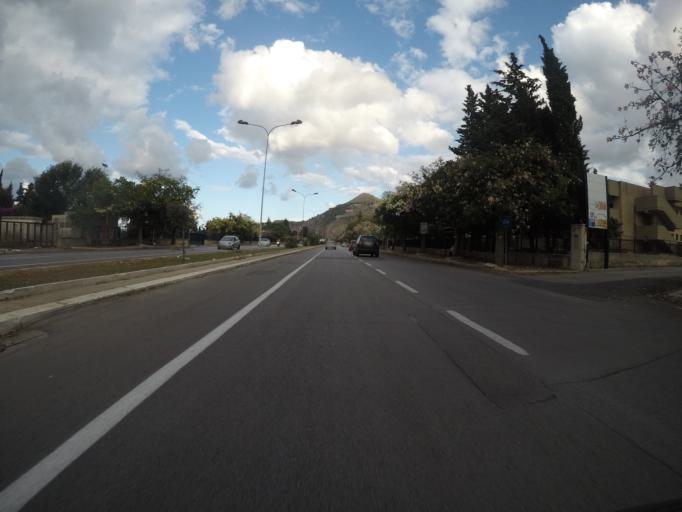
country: IT
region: Sicily
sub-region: Palermo
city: Palermo
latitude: 38.1889
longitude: 13.3164
